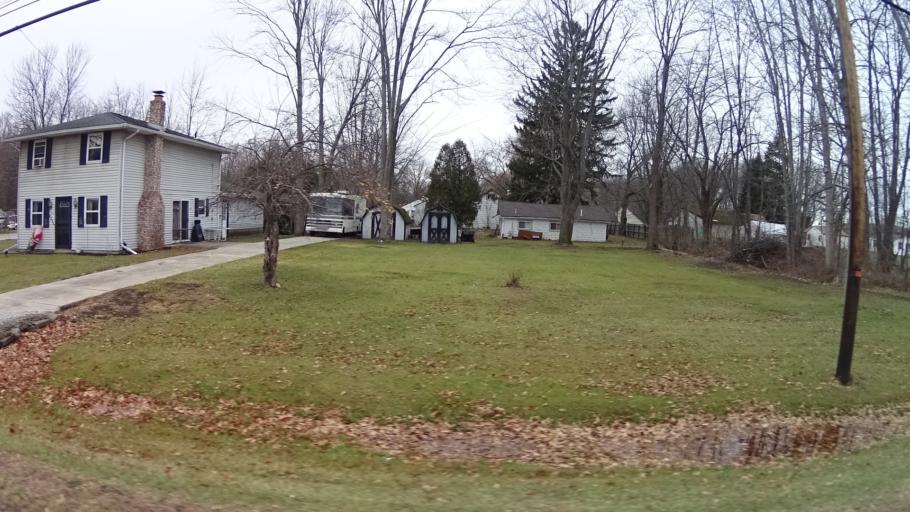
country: US
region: Ohio
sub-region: Lorain County
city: North Ridgeville
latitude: 41.3640
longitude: -82.0190
